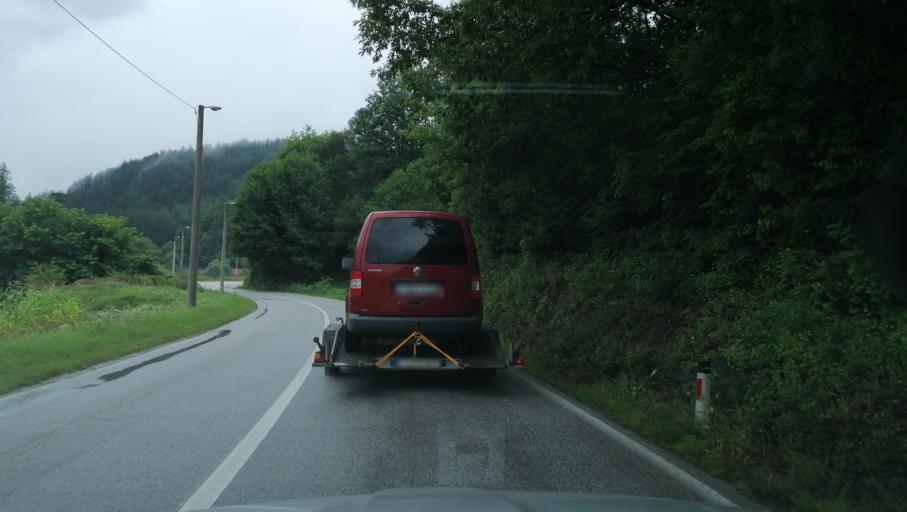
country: BA
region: Republika Srpska
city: Visegrad
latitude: 43.7819
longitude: 19.3590
